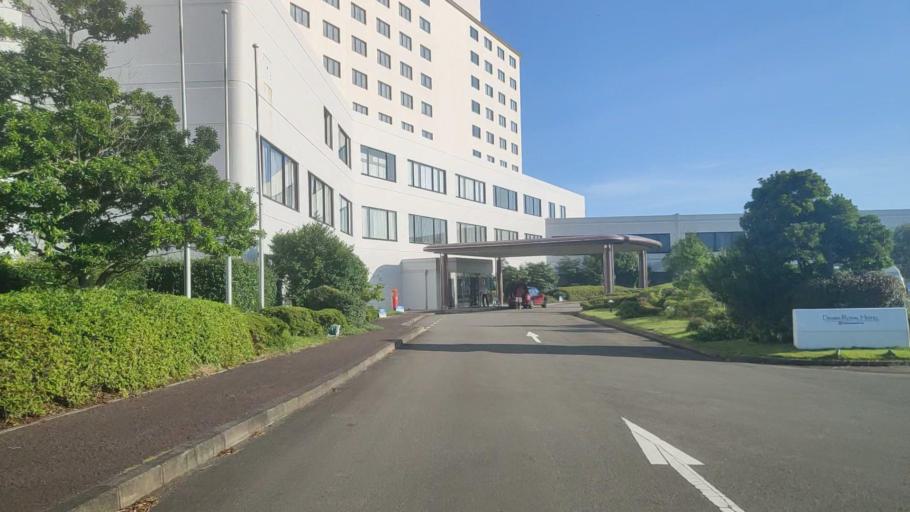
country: JP
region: Wakayama
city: Tanabe
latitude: 33.7689
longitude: 135.3019
